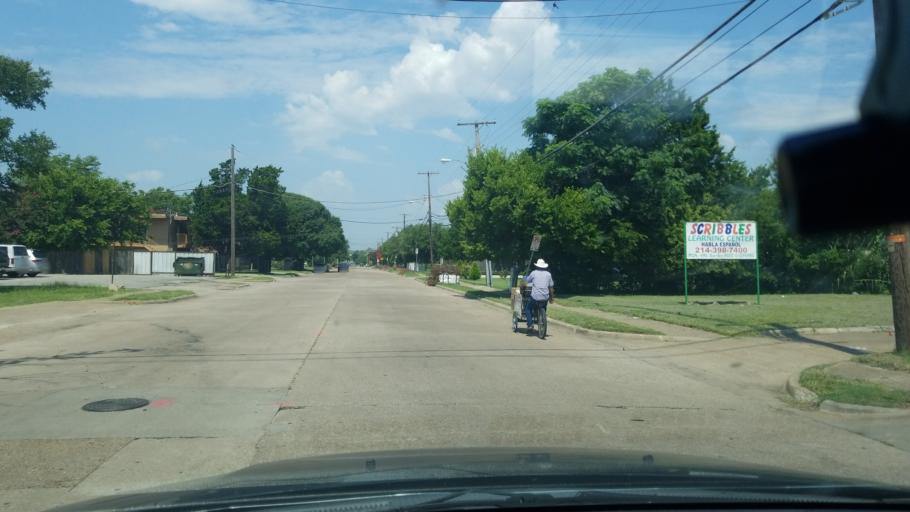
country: US
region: Texas
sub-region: Dallas County
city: Balch Springs
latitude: 32.7428
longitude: -96.6836
